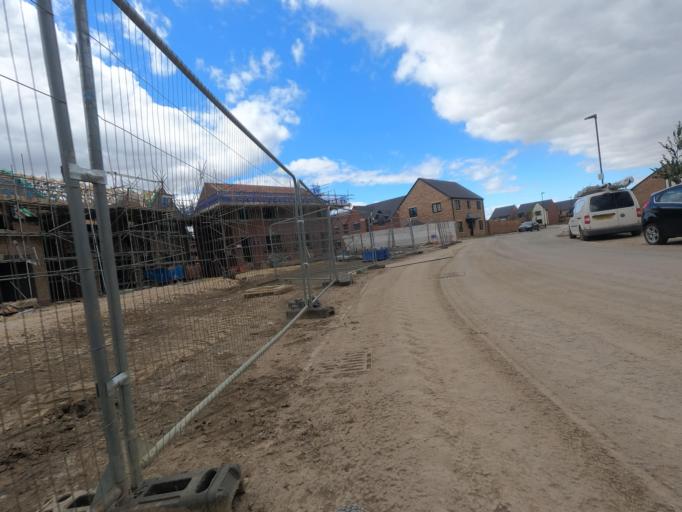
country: GB
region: England
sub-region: Northumberland
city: Seghill
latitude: 55.0364
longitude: -1.5867
